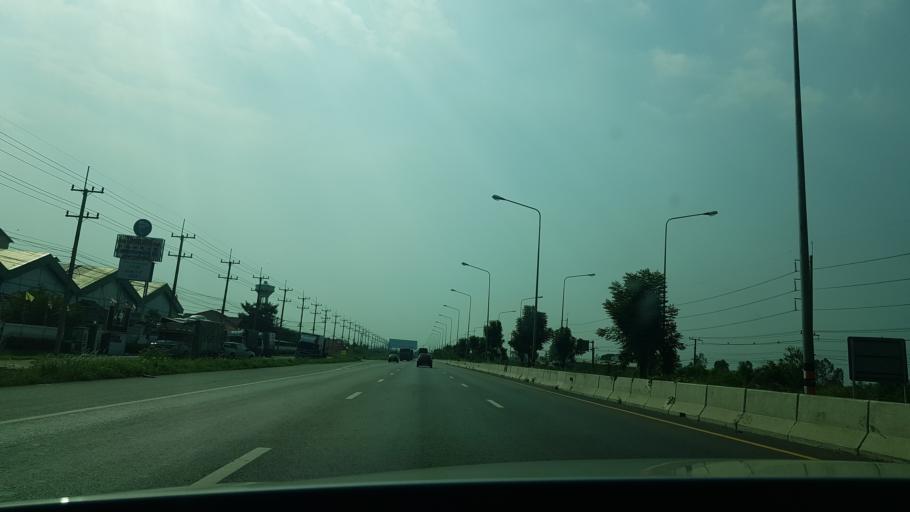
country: TH
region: Ratchaburi
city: Pak Tho
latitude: 13.3452
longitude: 99.8739
